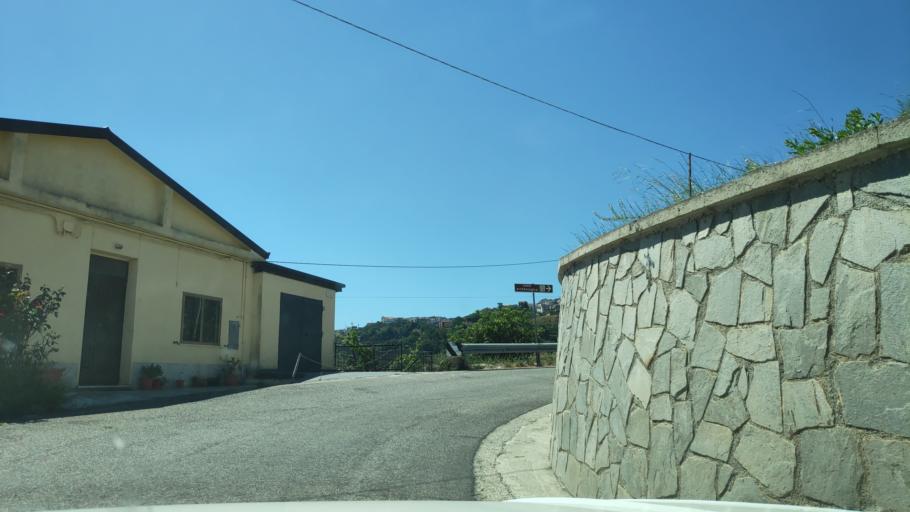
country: IT
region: Calabria
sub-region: Provincia di Catanzaro
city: Montauro
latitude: 38.7468
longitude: 16.5120
